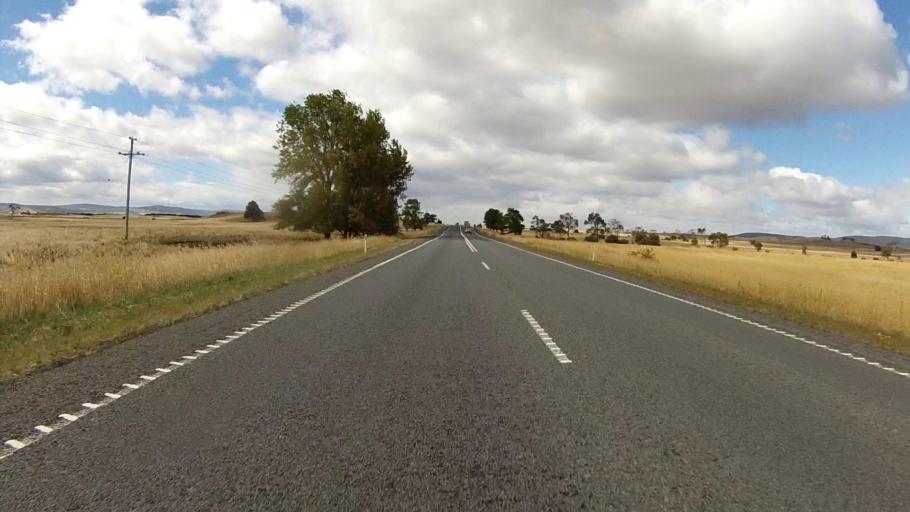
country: AU
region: Tasmania
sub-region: Northern Midlands
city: Evandale
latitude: -41.8655
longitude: 147.4579
